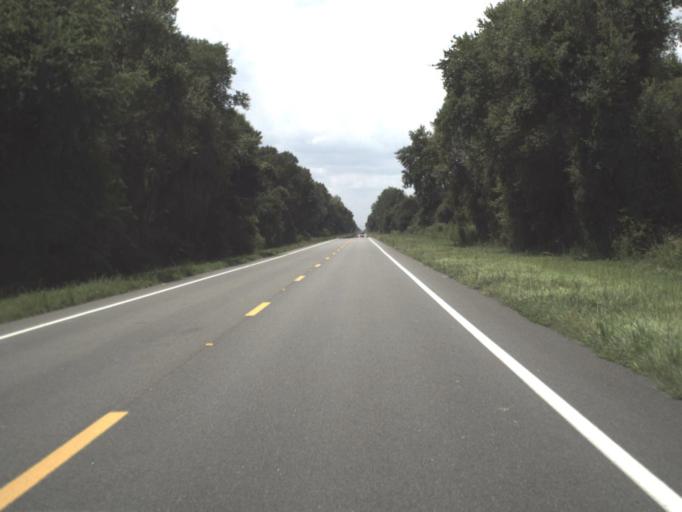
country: US
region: Florida
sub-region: Hamilton County
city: Jasper
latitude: 30.4202
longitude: -82.8555
